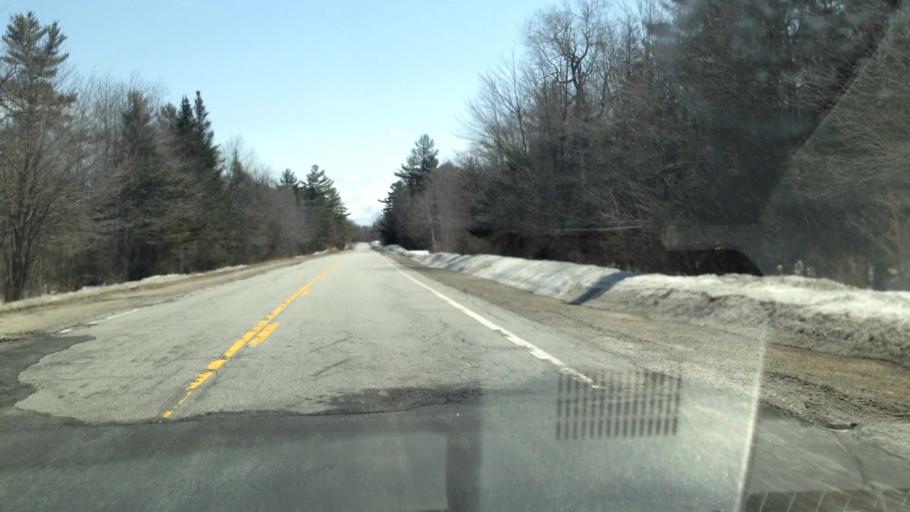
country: US
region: New Hampshire
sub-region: Sullivan County
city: Springfield
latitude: 43.4932
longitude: -71.9909
